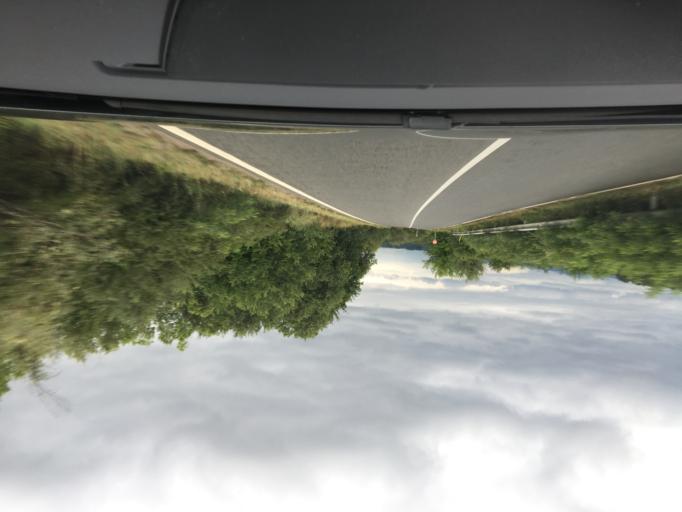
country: BG
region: Kyustendil
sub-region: Obshtina Boboshevo
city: Boboshevo
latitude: 42.2490
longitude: 22.8927
